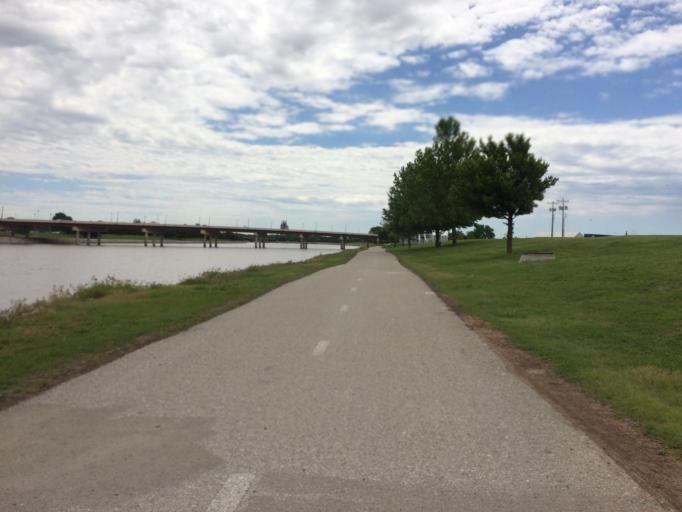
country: US
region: Oklahoma
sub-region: Oklahoma County
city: Oklahoma City
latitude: 35.4541
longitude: -97.5332
